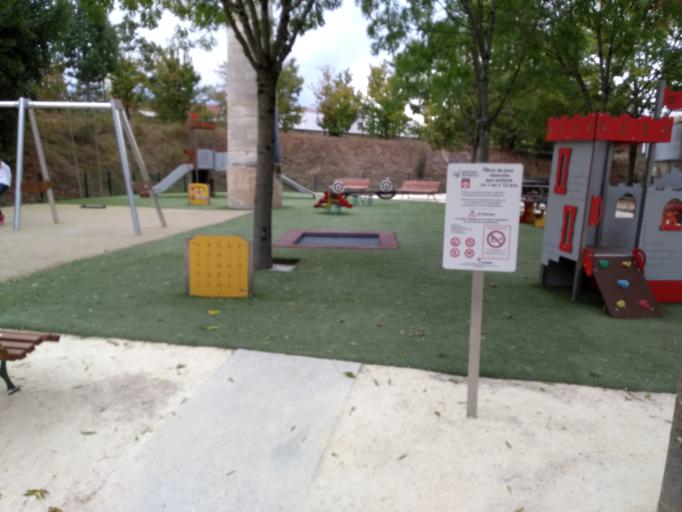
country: FR
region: Aquitaine
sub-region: Departement de la Gironde
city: Talence
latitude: 44.8266
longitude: -0.5996
